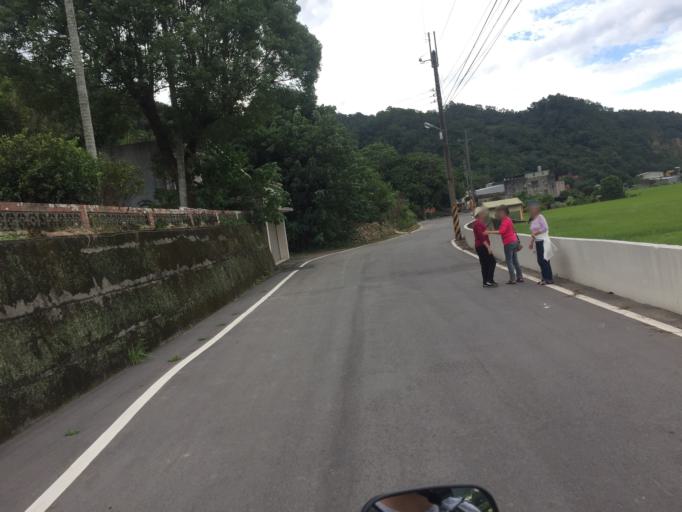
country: TW
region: Taiwan
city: Daxi
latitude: 24.7890
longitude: 121.1685
